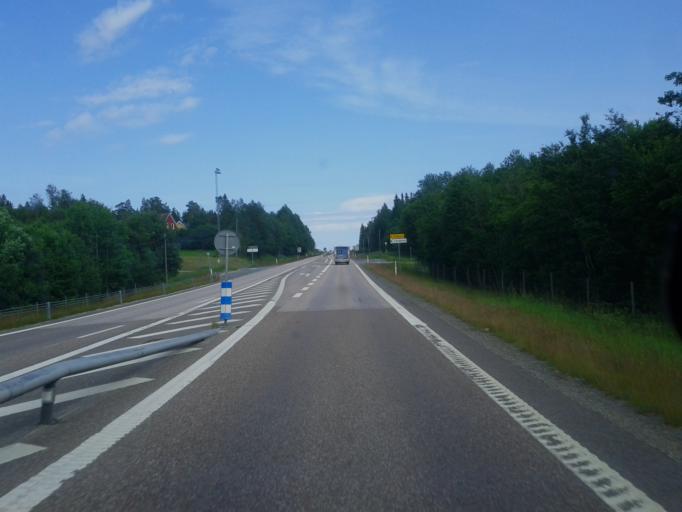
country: SE
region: Vaesternorrland
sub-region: OErnskoeldsviks Kommun
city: Husum
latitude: 63.3614
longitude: 19.1766
